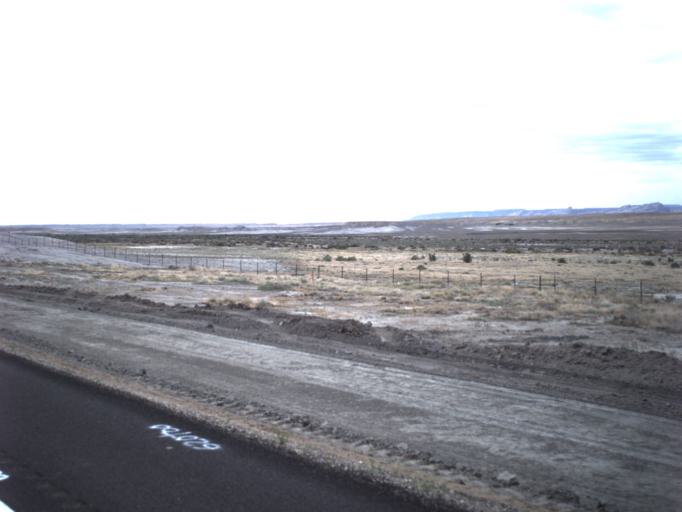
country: US
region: Utah
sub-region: Carbon County
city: East Carbon City
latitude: 39.0507
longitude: -110.3102
